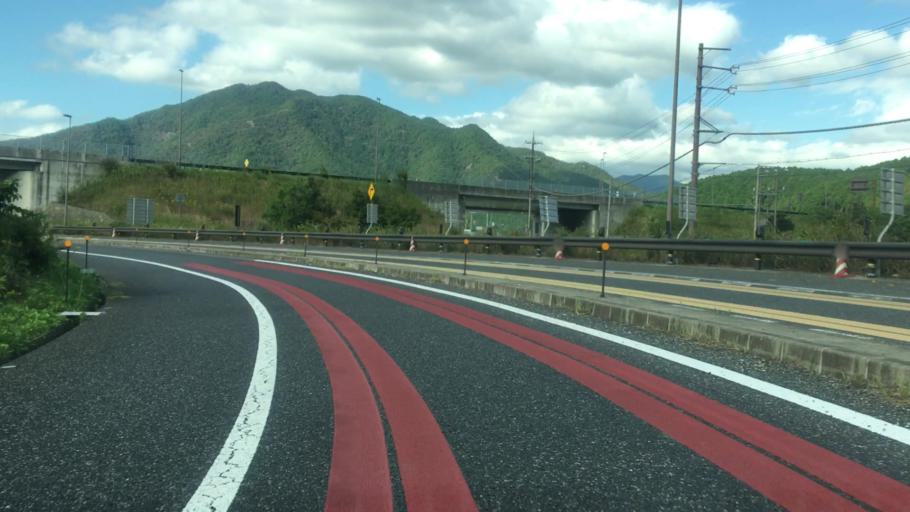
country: JP
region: Kyoto
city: Fukuchiyama
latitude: 35.1641
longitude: 135.0464
